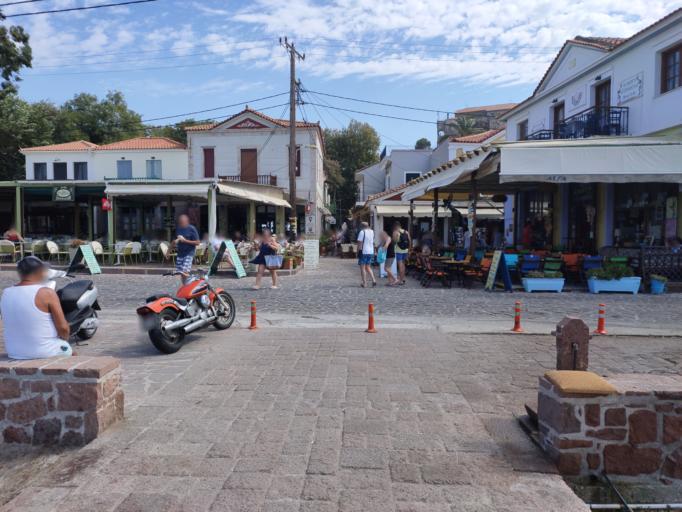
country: GR
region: North Aegean
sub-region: Nomos Lesvou
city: Petra
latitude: 39.3280
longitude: 26.1751
